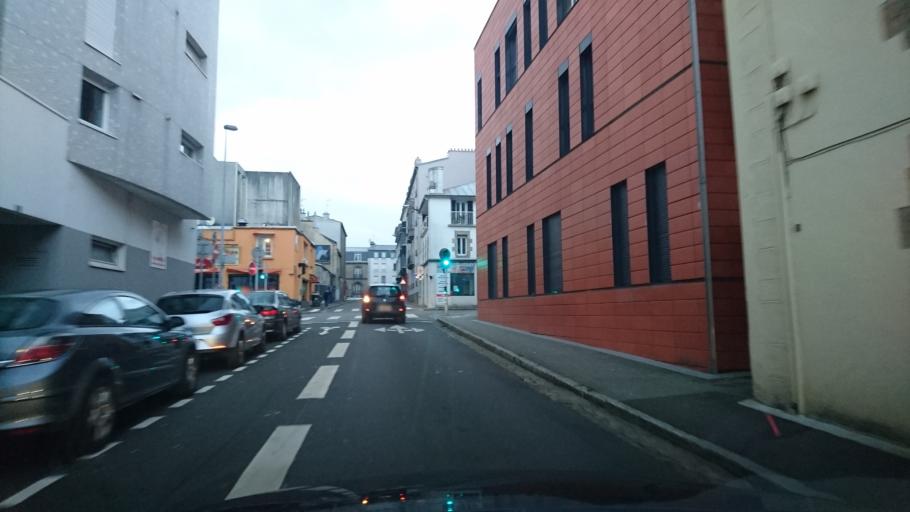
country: FR
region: Brittany
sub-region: Departement du Finistere
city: Brest
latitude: 48.3975
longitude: -4.4725
